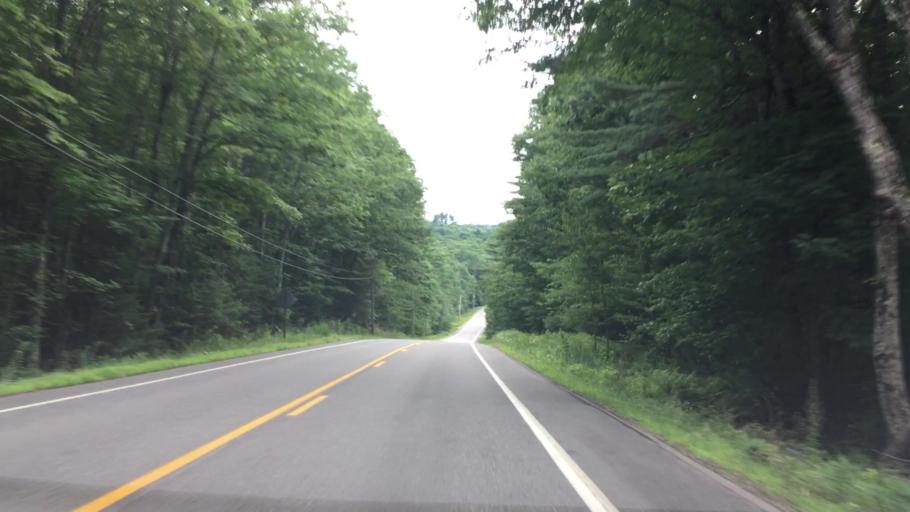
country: US
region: Maine
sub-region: Waldo County
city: Lincolnville
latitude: 44.3332
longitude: -69.0582
